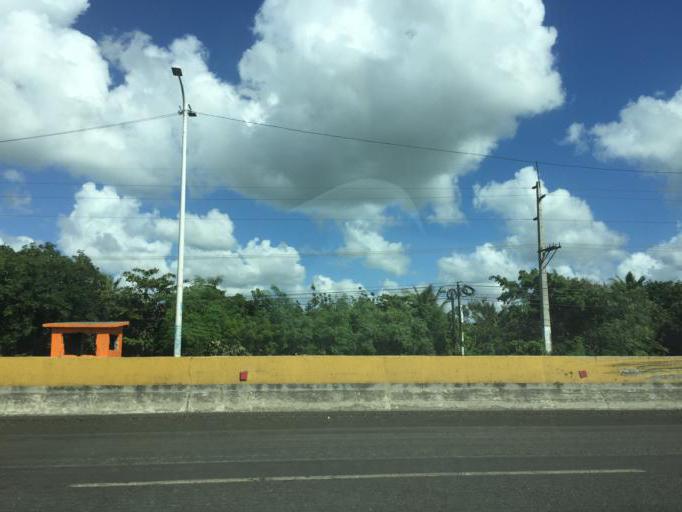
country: DO
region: Santo Domingo
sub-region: Santo Domingo
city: Boca Chica
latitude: 18.4550
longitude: -69.6984
